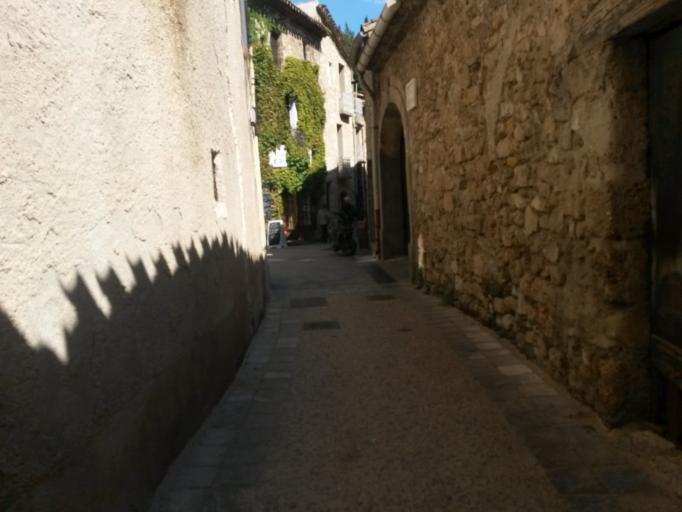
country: FR
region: Languedoc-Roussillon
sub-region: Departement de l'Herault
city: Saint-Jean-de-Fos
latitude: 43.7337
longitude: 3.5517
